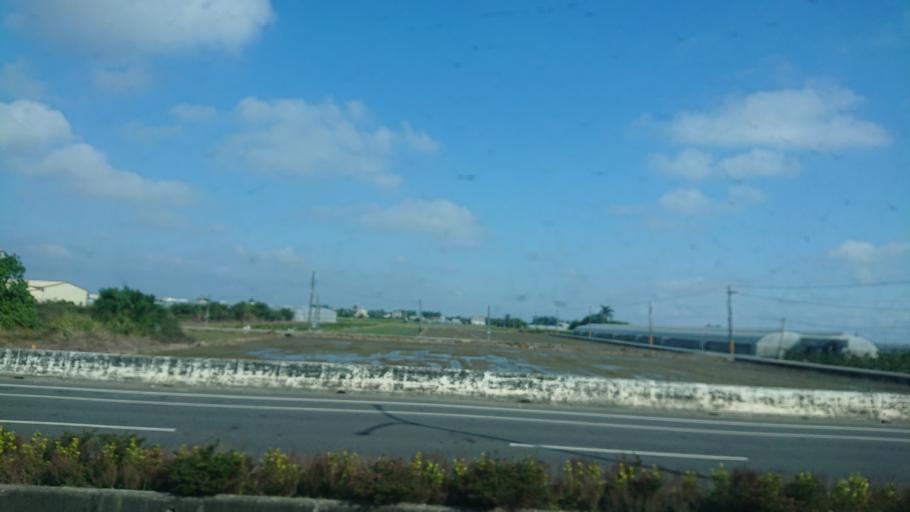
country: TW
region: Taiwan
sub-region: Chiayi
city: Taibao
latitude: 23.4582
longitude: 120.3057
